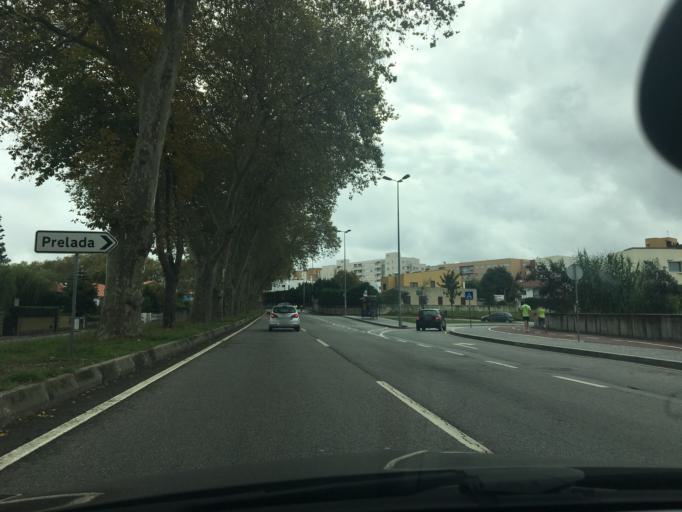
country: PT
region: Porto
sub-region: Matosinhos
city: Senhora da Hora
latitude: 41.1802
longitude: -8.6345
